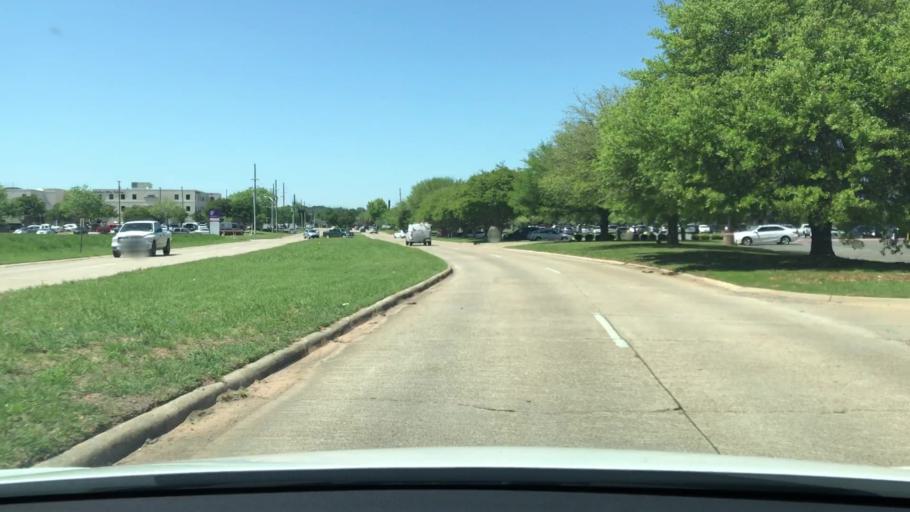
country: US
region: Louisiana
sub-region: Bossier Parish
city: Bossier City
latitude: 32.4250
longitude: -93.7136
